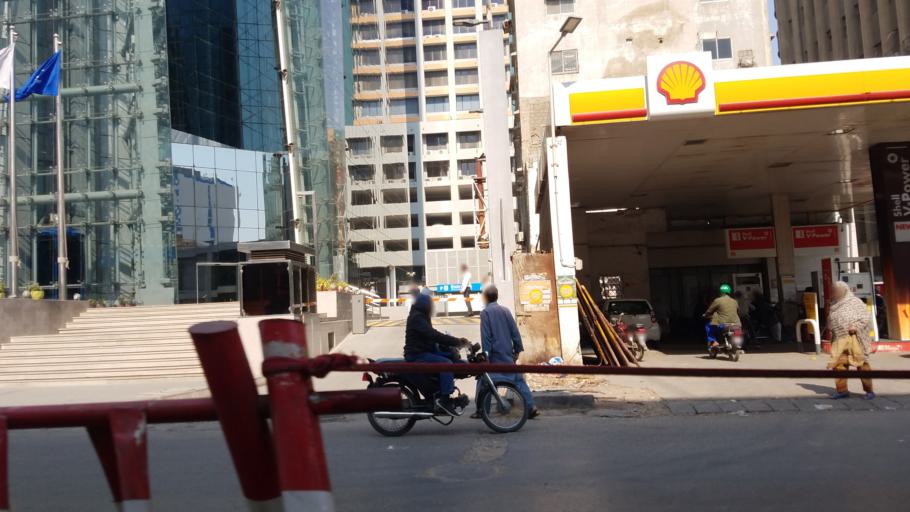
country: PK
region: Sindh
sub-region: Karachi District
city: Karachi
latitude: 24.8495
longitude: 67.0038
